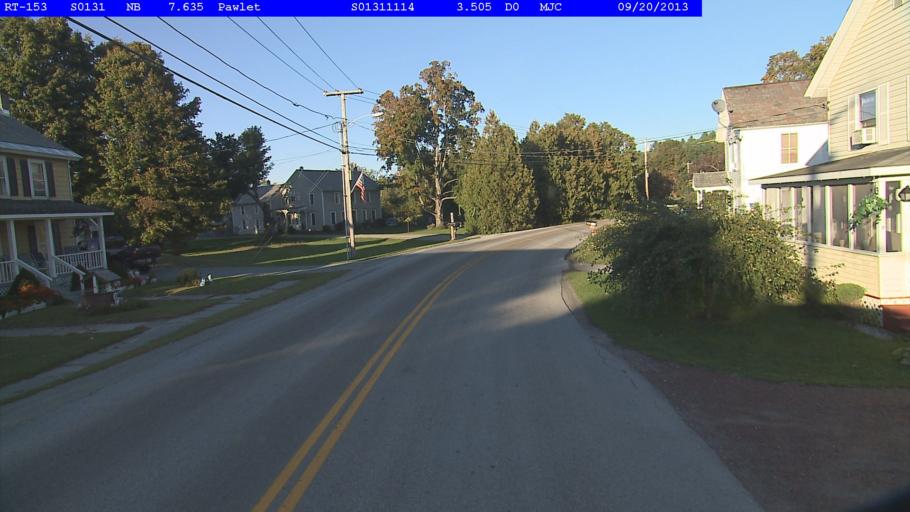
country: US
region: New York
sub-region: Washington County
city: Granville
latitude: 43.3607
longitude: -73.2451
